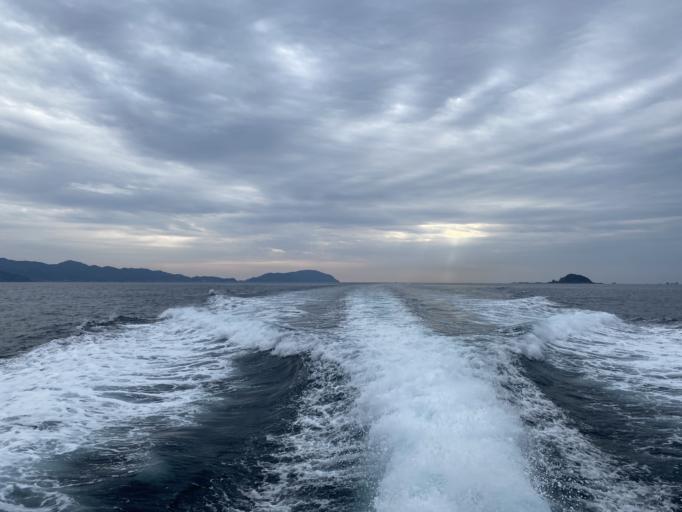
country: JP
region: Nagasaki
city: Nagasaki-shi
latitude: 32.6558
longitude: 129.7722
